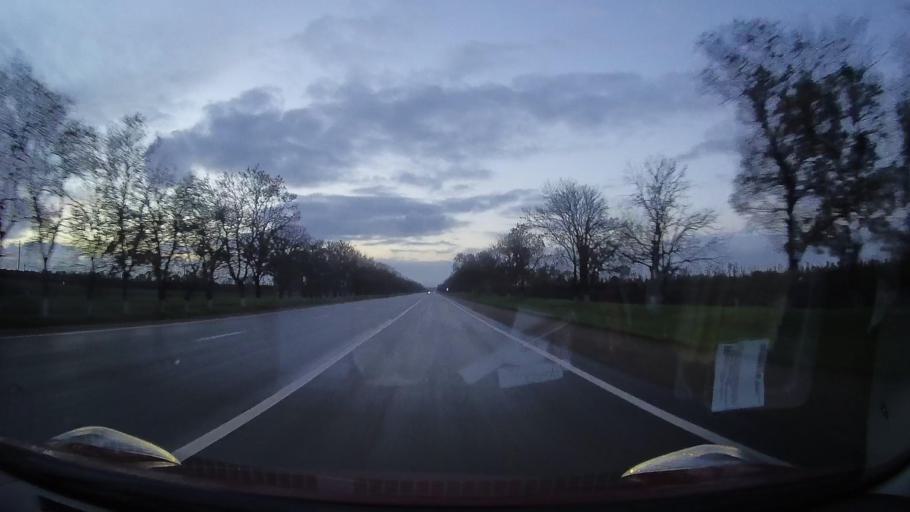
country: RU
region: Krasnodarskiy
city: Zavetnyy
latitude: 44.9003
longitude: 41.1860
